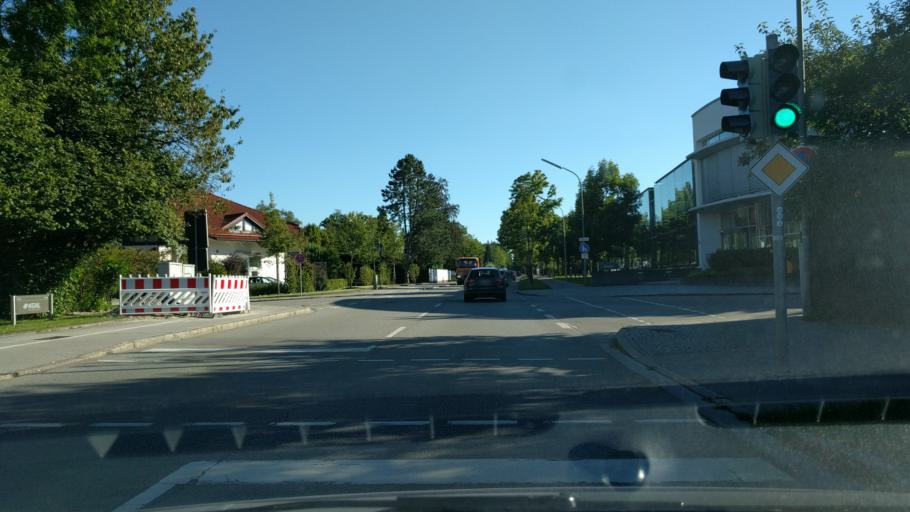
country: DE
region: Bavaria
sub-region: Upper Bavaria
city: Grunwald
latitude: 48.0354
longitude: 11.5213
